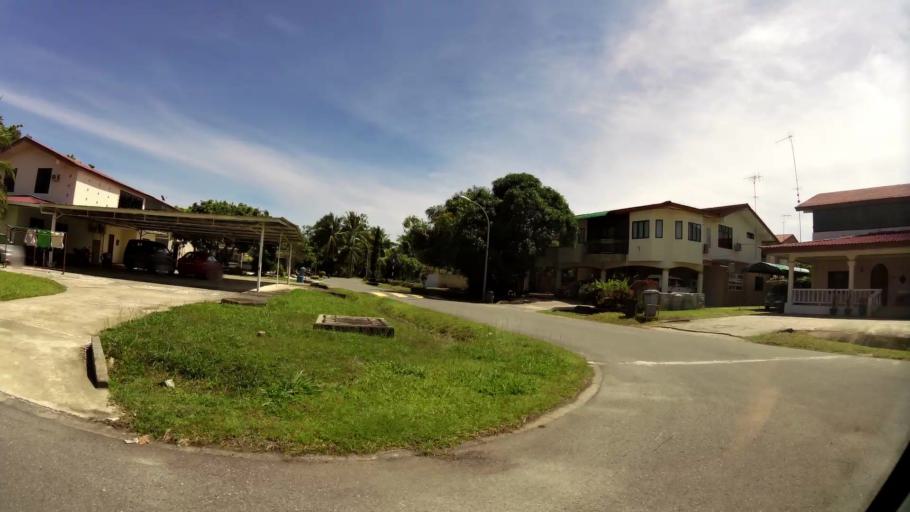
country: BN
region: Belait
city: Kuala Belait
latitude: 4.5873
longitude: 114.2247
